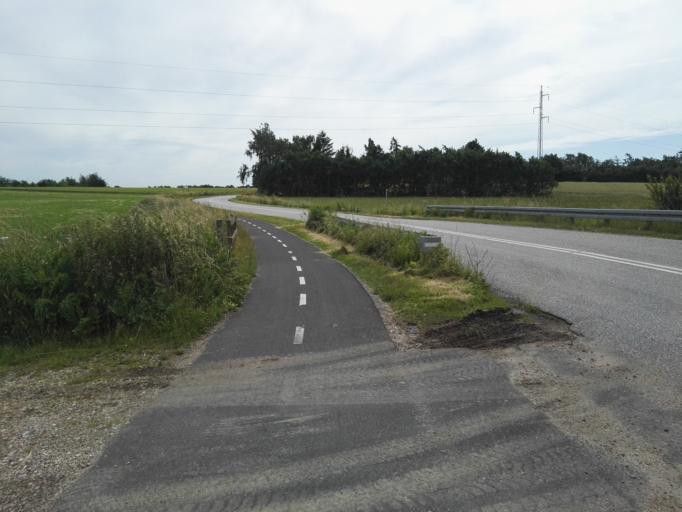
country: DK
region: Capital Region
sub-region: Hillerod Kommune
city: Skaevinge
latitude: 55.9000
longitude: 12.1512
